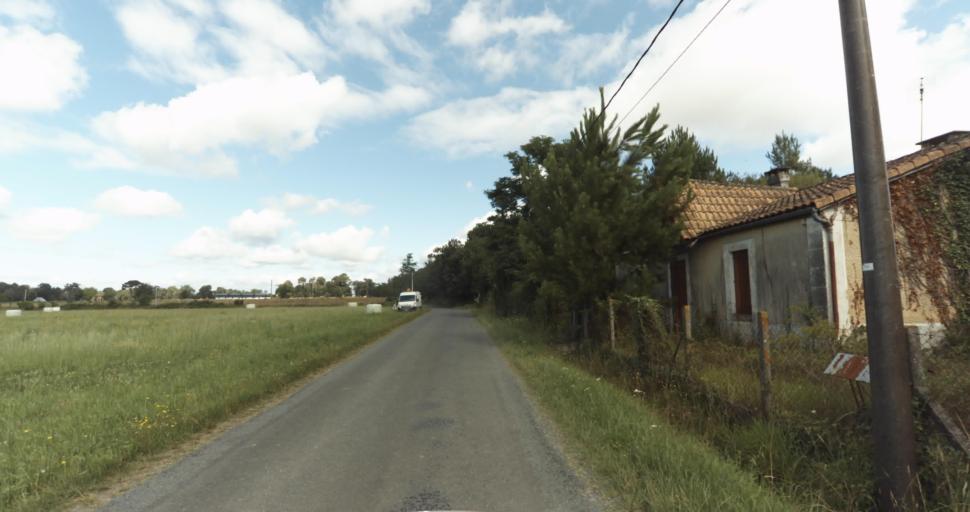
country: FR
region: Aquitaine
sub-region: Departement de la Gironde
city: Bazas
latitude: 44.4565
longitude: -0.1938
